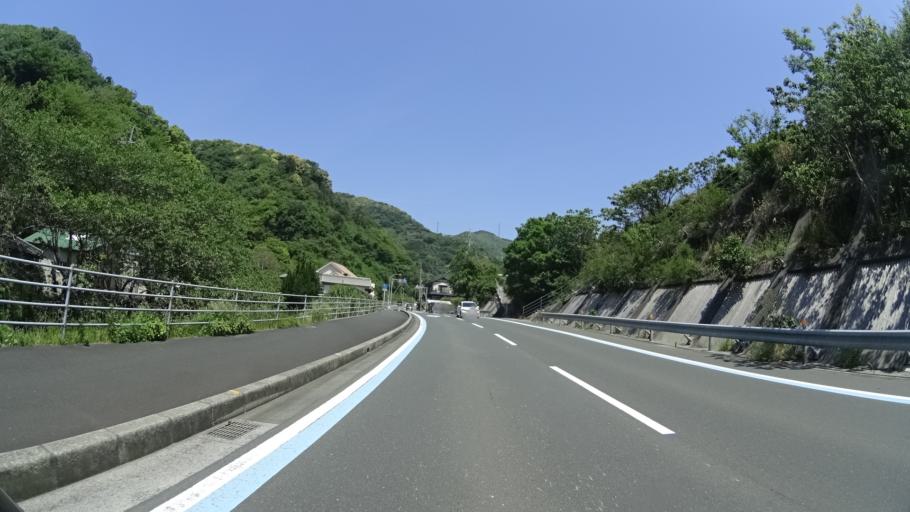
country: JP
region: Ehime
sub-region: Nishiuwa-gun
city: Ikata-cho
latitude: 33.4990
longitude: 132.3970
